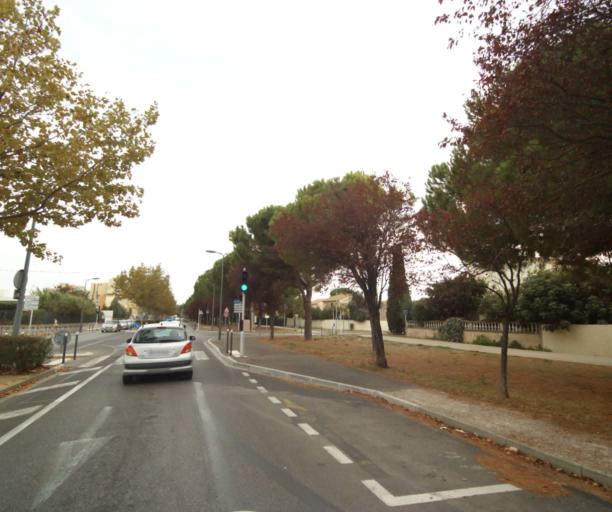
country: FR
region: Provence-Alpes-Cote d'Azur
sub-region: Departement des Bouches-du-Rhone
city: Marignane
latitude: 43.4143
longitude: 5.2043
